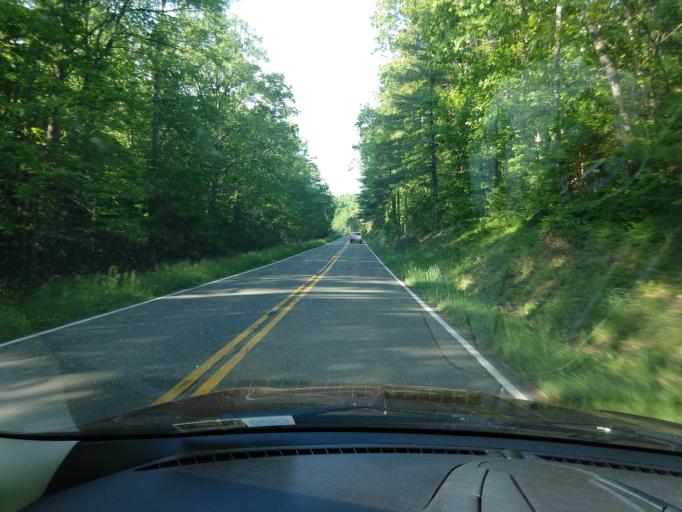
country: US
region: Virginia
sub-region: City of Galax
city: Galax
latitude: 36.7260
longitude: -80.9840
